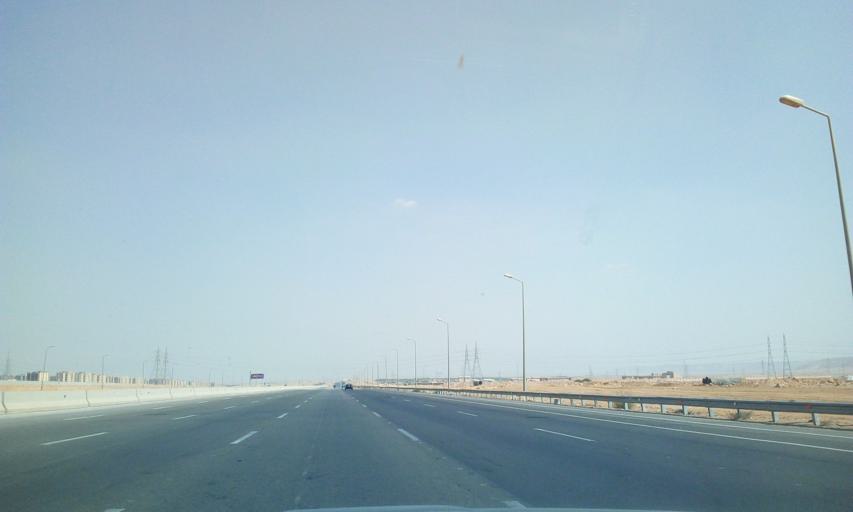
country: EG
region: Muhafazat al Qahirah
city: Halwan
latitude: 29.9200
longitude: 31.6212
